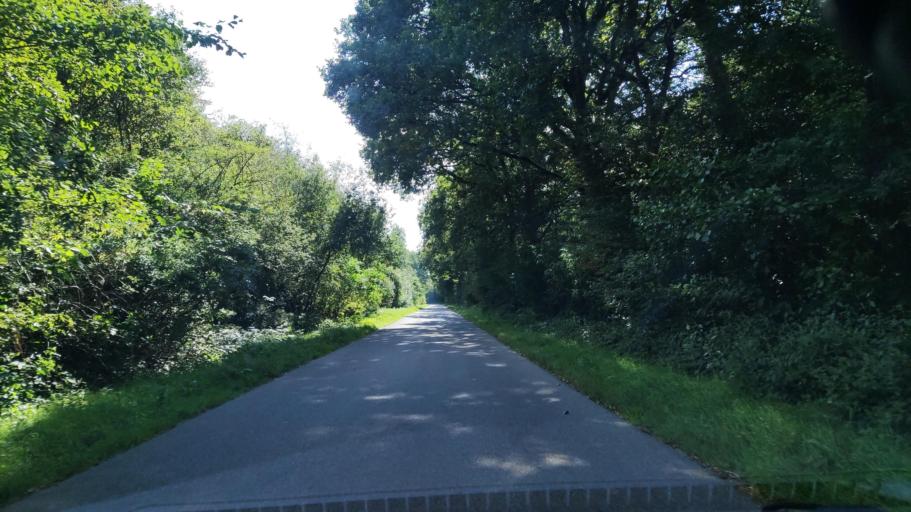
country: DE
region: Schleswig-Holstein
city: Brammer
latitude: 54.2148
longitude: 9.7202
